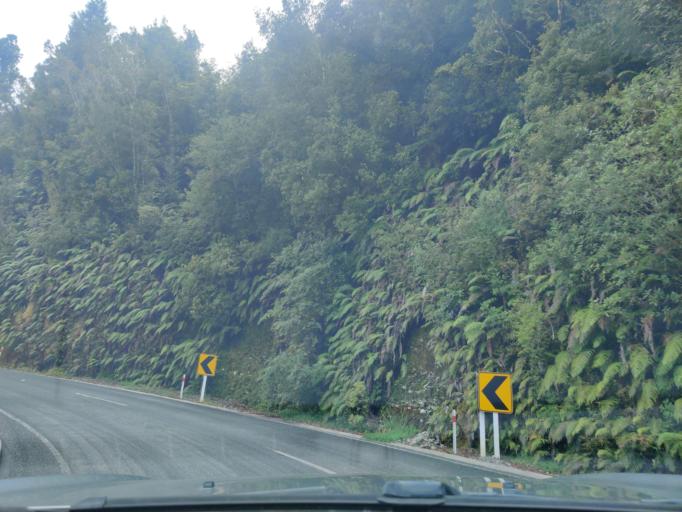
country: NZ
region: West Coast
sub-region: Westland District
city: Hokitika
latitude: -43.1769
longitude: 170.4557
